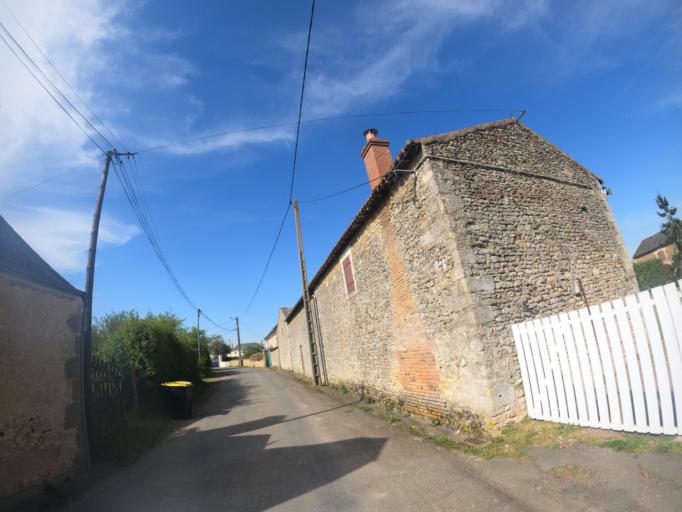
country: FR
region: Poitou-Charentes
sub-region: Departement des Deux-Sevres
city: Saint-Varent
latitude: 46.9256
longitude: -0.2216
